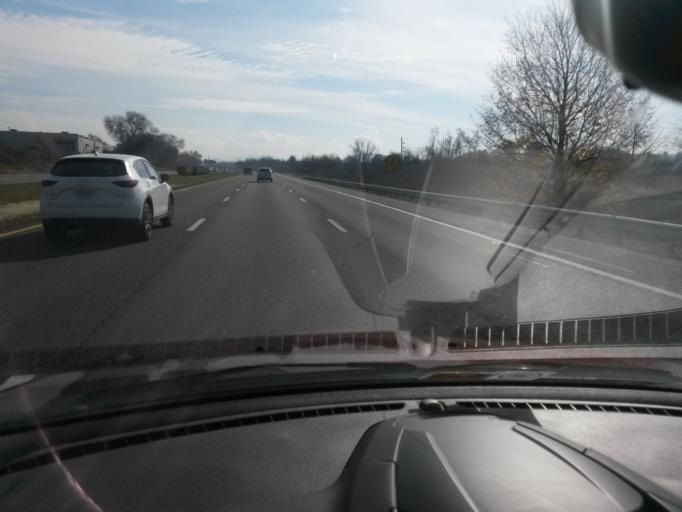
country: US
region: Virginia
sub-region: Roanoke County
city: Hollins
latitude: 37.3077
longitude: -79.9729
